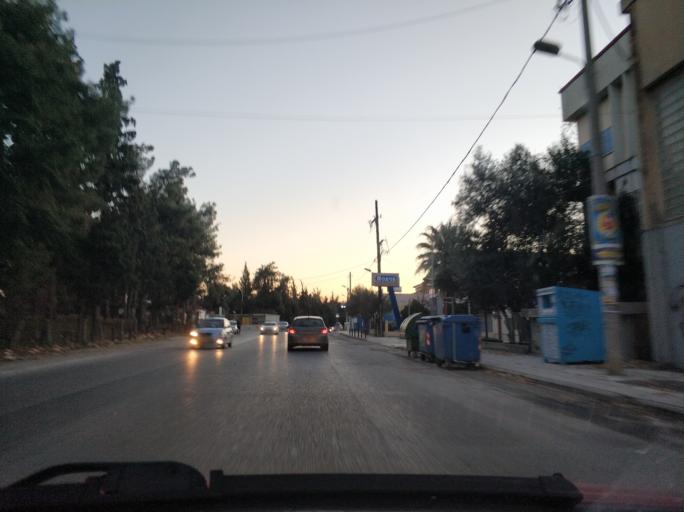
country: GR
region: Central Macedonia
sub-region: Nomos Thessalonikis
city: Stavroupoli
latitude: 40.6762
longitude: 22.9453
